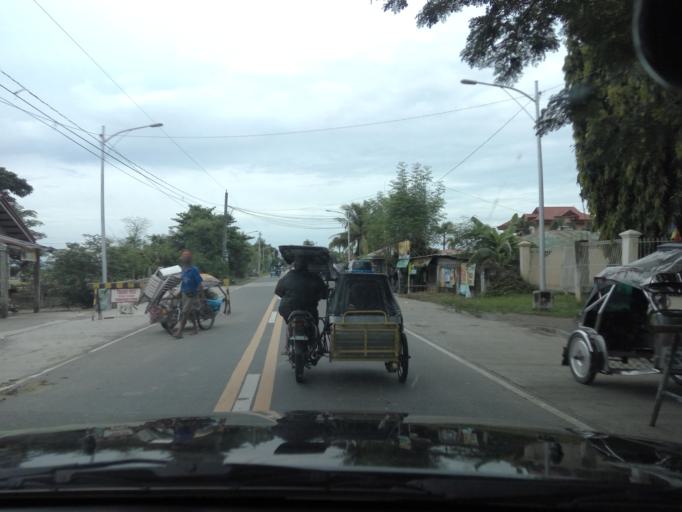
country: PH
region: Central Luzon
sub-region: Province of Nueva Ecija
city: Carmen
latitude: 15.4459
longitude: 120.8283
